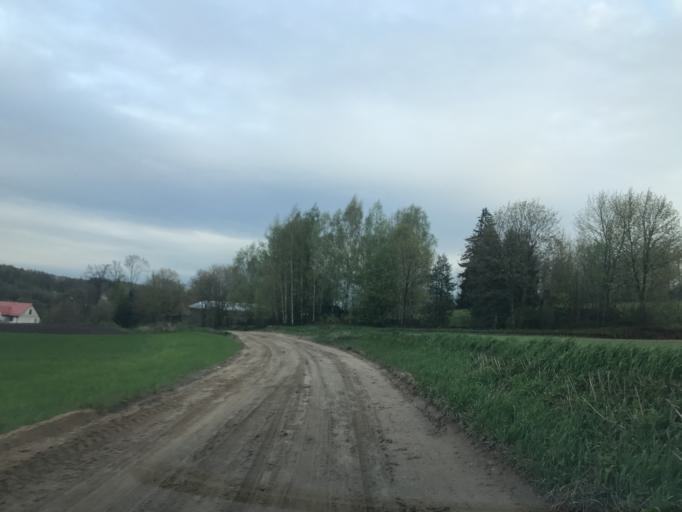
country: PL
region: Warmian-Masurian Voivodeship
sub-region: Powiat ilawski
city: Lubawa
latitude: 53.5333
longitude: 19.8962
